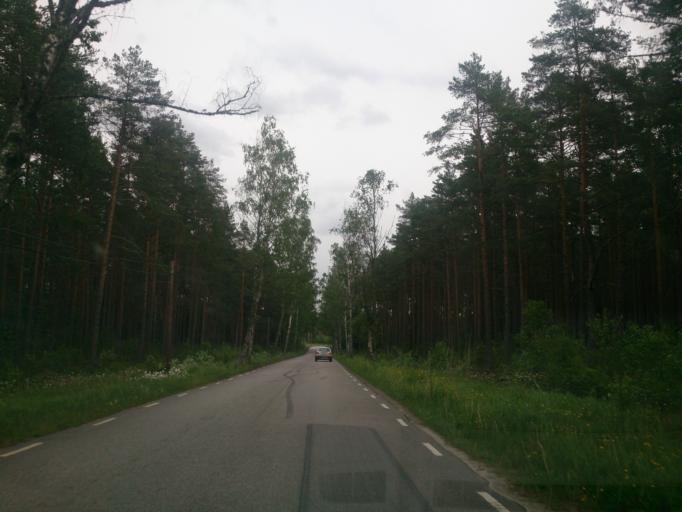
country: SE
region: OEstergoetland
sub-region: Valdemarsviks Kommun
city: Gusum
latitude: 58.3300
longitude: 16.4096
